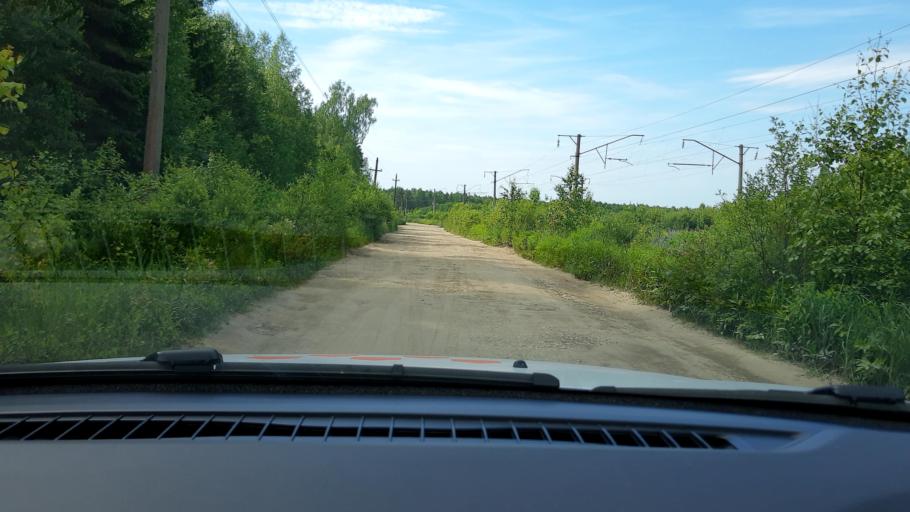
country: RU
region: Nizjnij Novgorod
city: Linda
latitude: 56.6679
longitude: 44.1687
